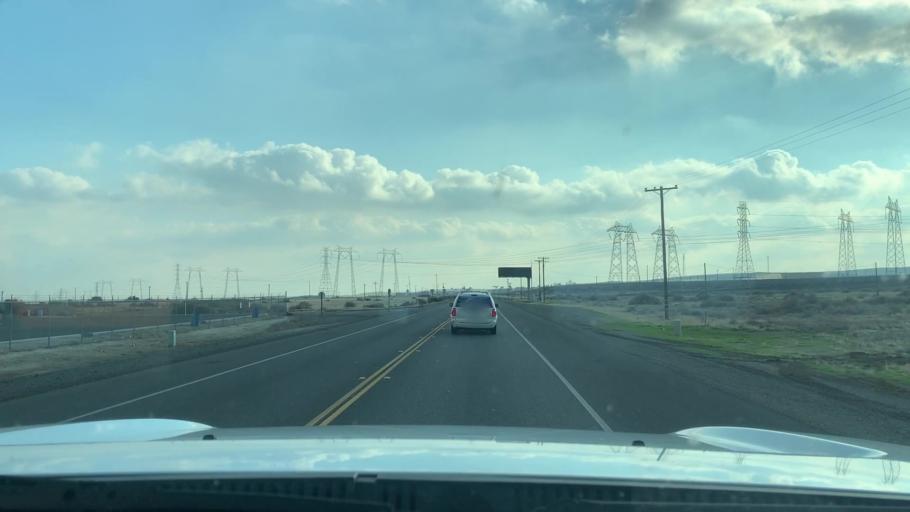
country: US
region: California
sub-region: Kings County
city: Kettleman City
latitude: 36.0037
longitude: -119.9595
